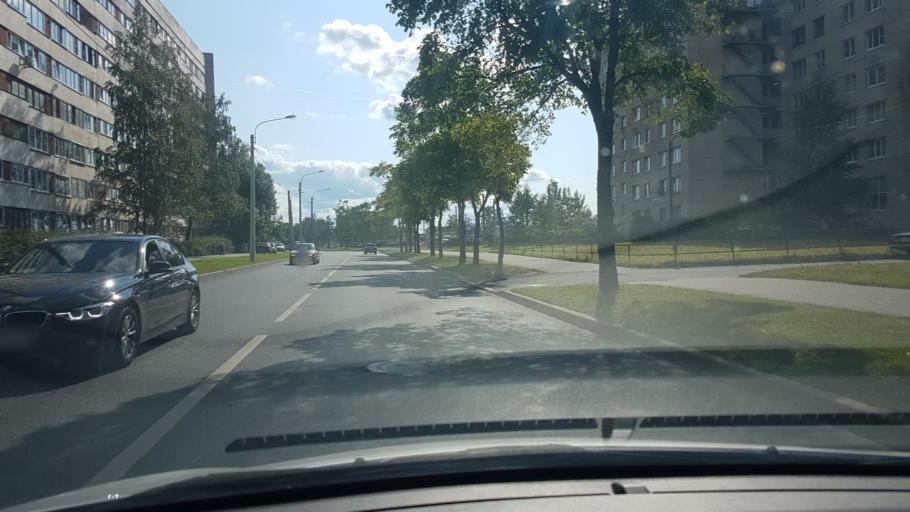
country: RU
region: St.-Petersburg
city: Sosnovaya Polyana
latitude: 59.8378
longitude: 30.1281
